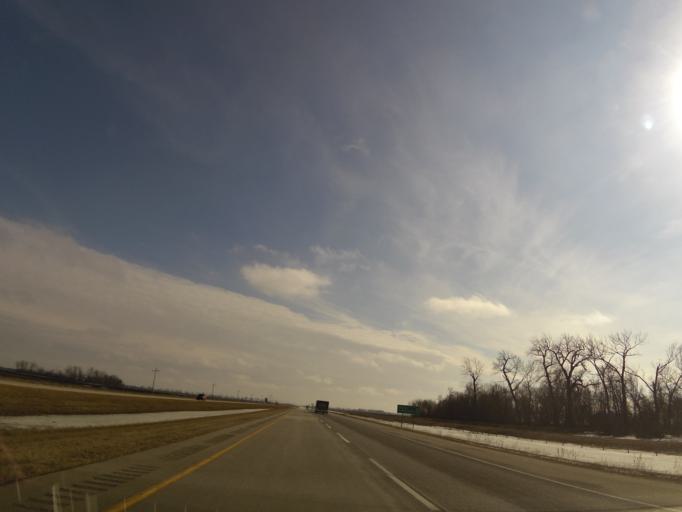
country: US
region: North Dakota
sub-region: Grand Forks County
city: Grand Forks Air Force Base
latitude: 48.1889
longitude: -97.1895
